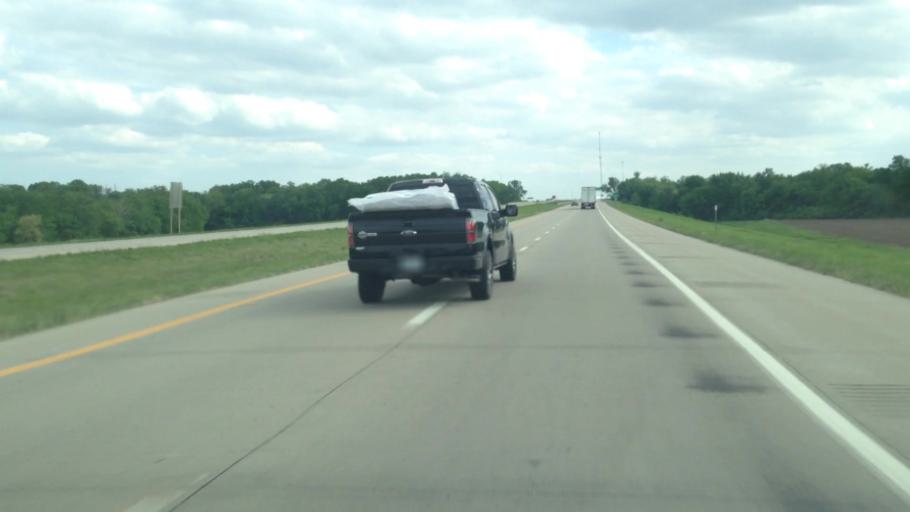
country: US
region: Kansas
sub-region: Franklin County
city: Ottawa
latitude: 38.6045
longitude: -95.2329
